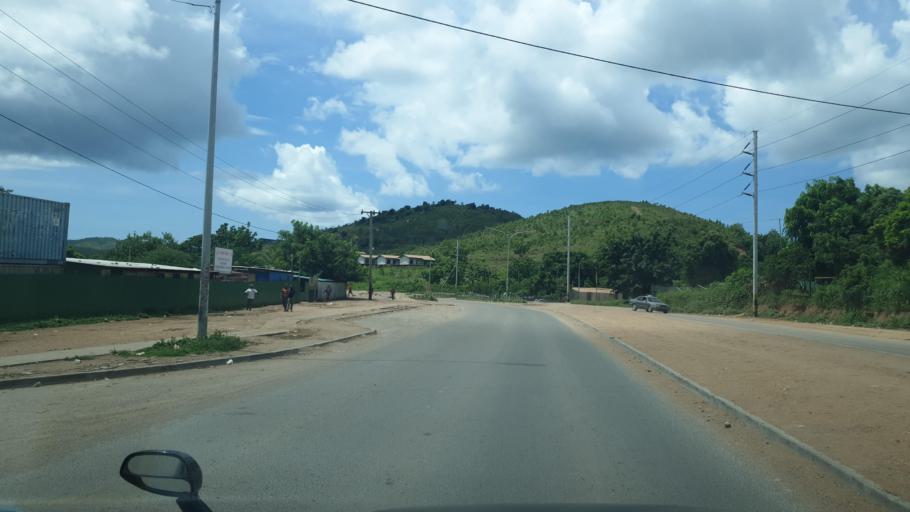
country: PG
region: National Capital
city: Port Moresby
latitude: -9.3884
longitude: 147.1538
